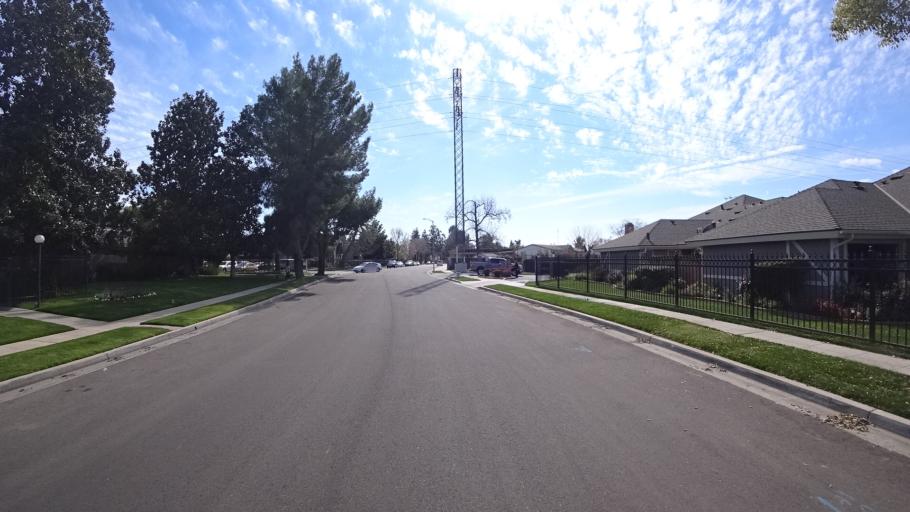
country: US
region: California
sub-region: Fresno County
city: Clovis
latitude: 36.8507
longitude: -119.7792
